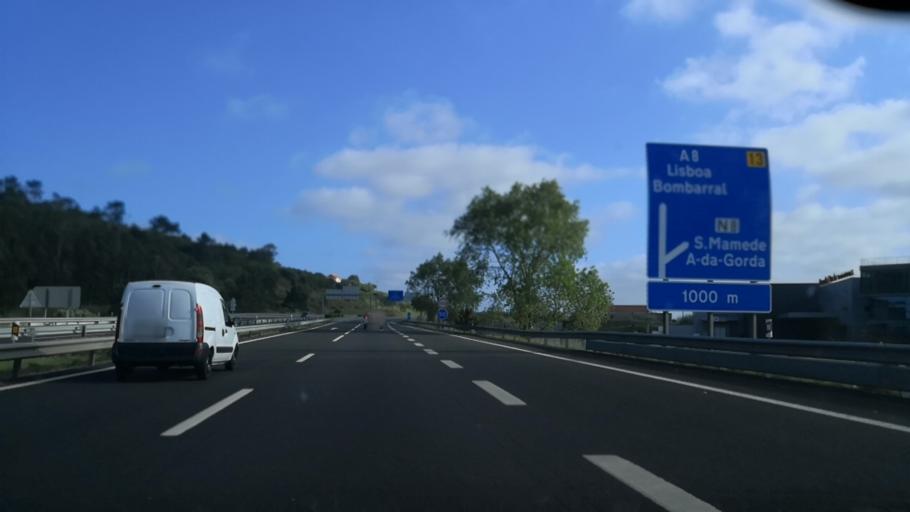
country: PT
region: Leiria
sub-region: Obidos
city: Obidos
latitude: 39.3356
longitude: -9.1745
